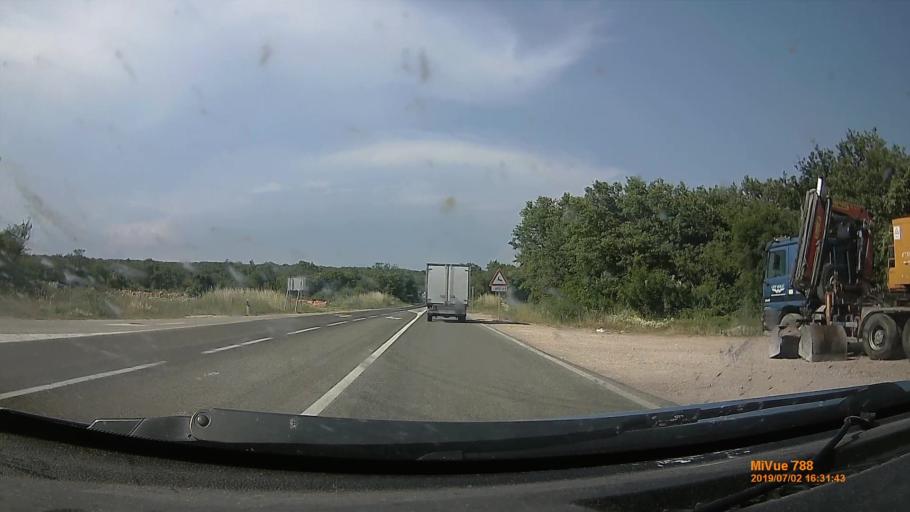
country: HR
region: Primorsko-Goranska
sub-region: Grad Krk
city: Krk
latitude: 45.0566
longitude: 14.4874
